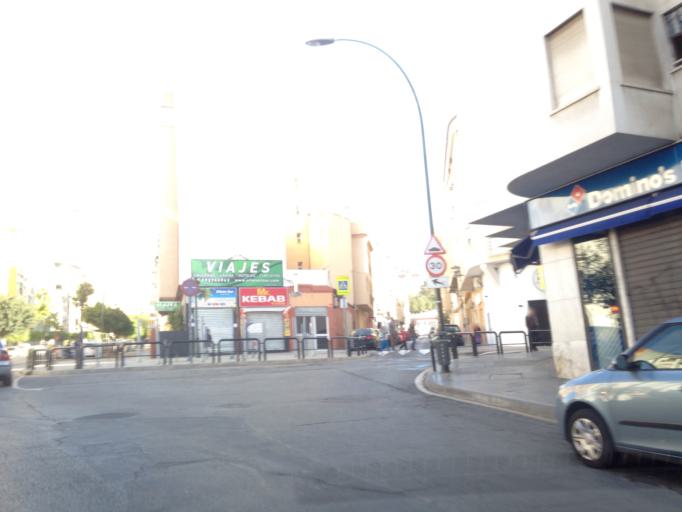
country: ES
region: Andalusia
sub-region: Provincia de Malaga
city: Malaga
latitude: 36.7332
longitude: -4.4156
